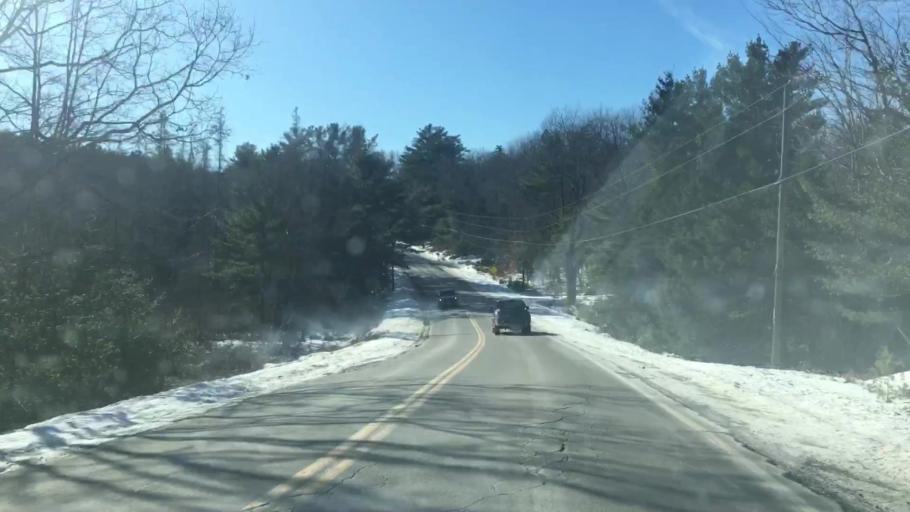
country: US
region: Maine
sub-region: Hancock County
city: Sedgwick
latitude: 44.3977
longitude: -68.6358
